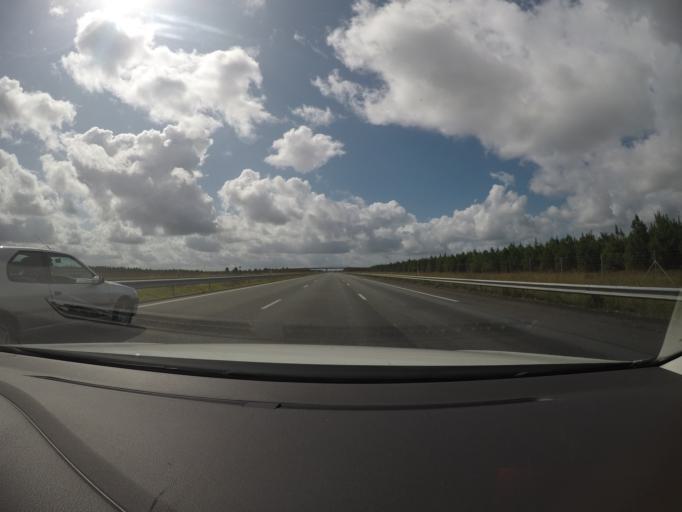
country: FR
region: Aquitaine
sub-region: Departement des Landes
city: Labouheyre
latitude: 44.1858
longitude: -0.9403
